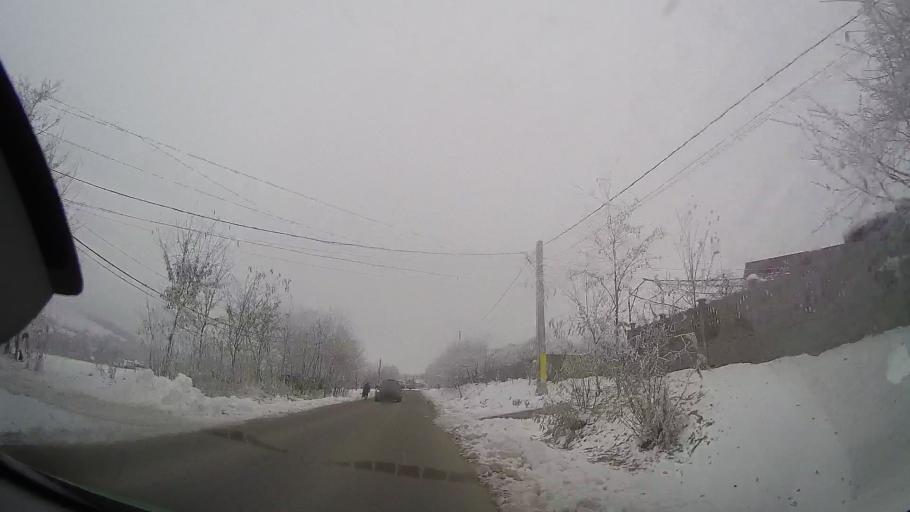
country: RO
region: Neamt
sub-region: Comuna Icusesti
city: Balusesti
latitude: 46.8679
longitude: 26.9941
